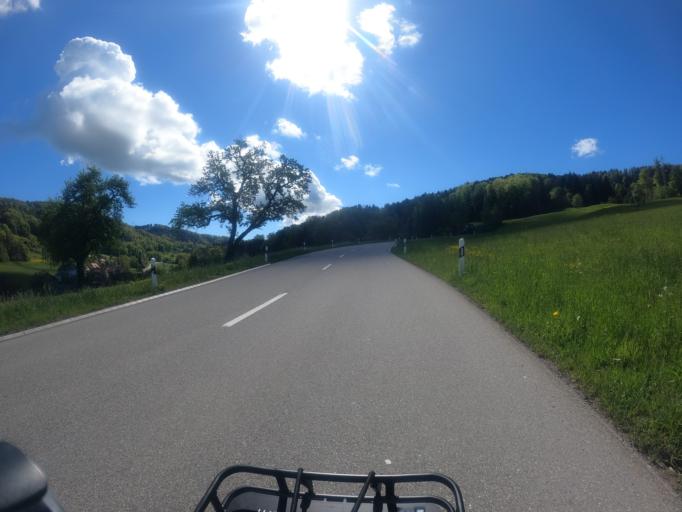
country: CH
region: Zurich
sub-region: Bezirk Affoltern
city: Affoltern / Sonnenberg
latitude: 47.2833
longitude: 8.4842
